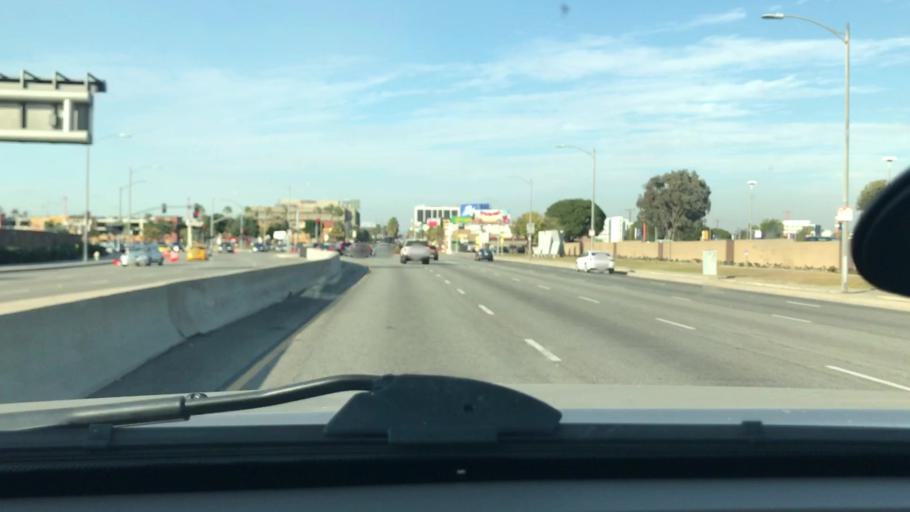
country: US
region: California
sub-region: Los Angeles County
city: El Segundo
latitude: 33.9508
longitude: -118.3962
